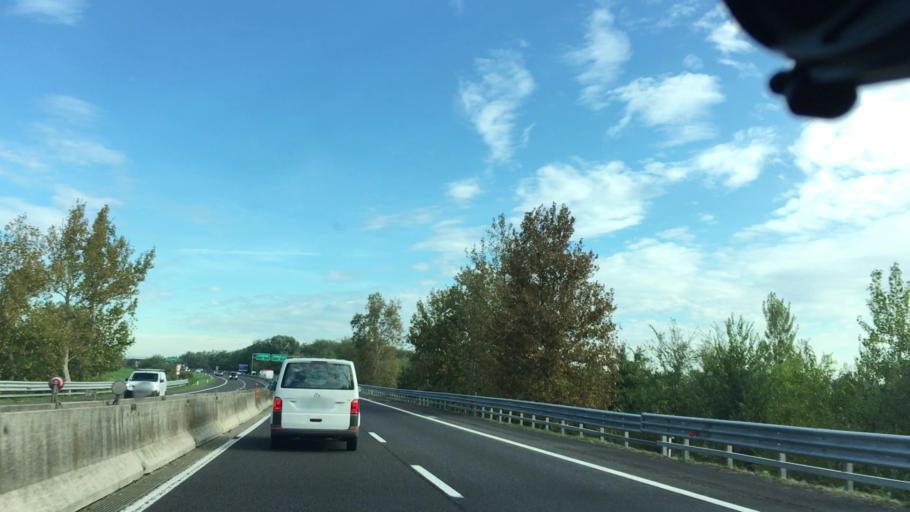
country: IT
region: Emilia-Romagna
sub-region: Provincia di Ferrara
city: Porotto-Cassama
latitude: 44.8562
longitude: 11.5691
